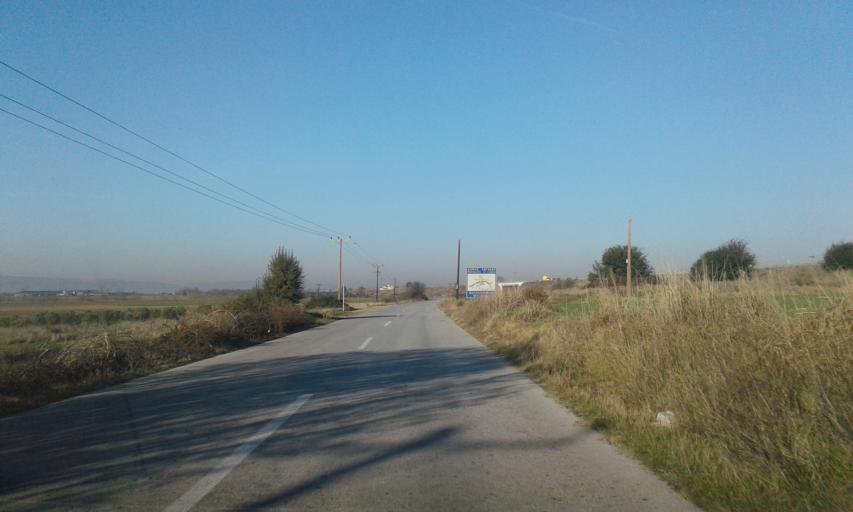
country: GR
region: Central Macedonia
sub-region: Nomos Thessalonikis
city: Kolchikon
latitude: 40.7076
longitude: 23.1863
